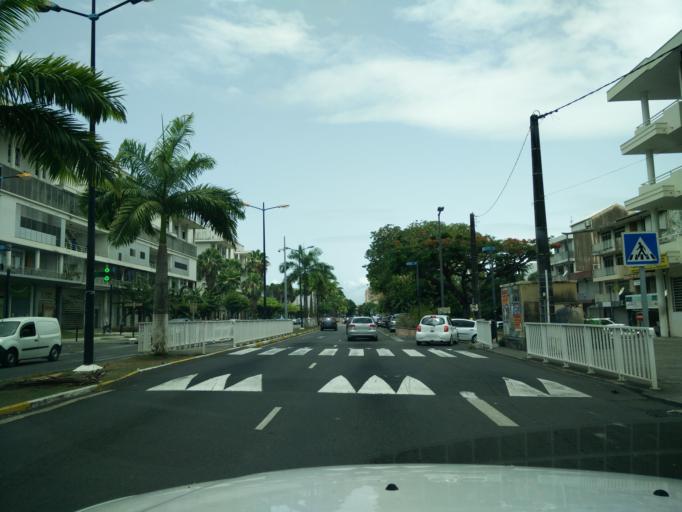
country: GP
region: Guadeloupe
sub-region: Guadeloupe
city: Pointe-a-Pitre
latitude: 16.2456
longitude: -61.5299
